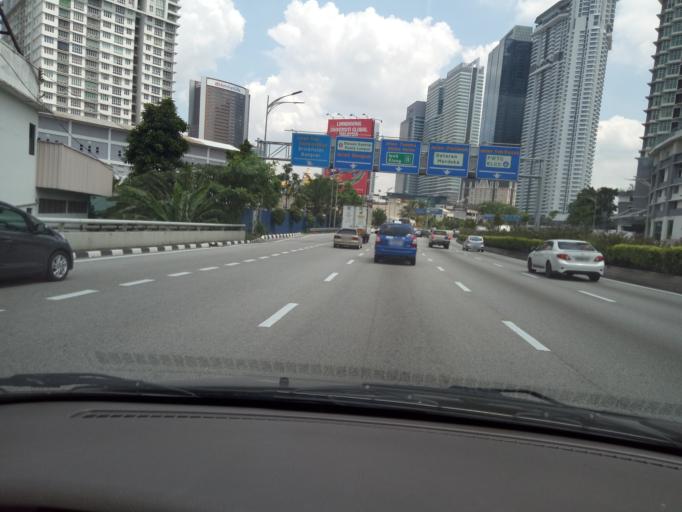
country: MY
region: Kuala Lumpur
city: Kuala Lumpur
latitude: 3.1354
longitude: 101.6939
